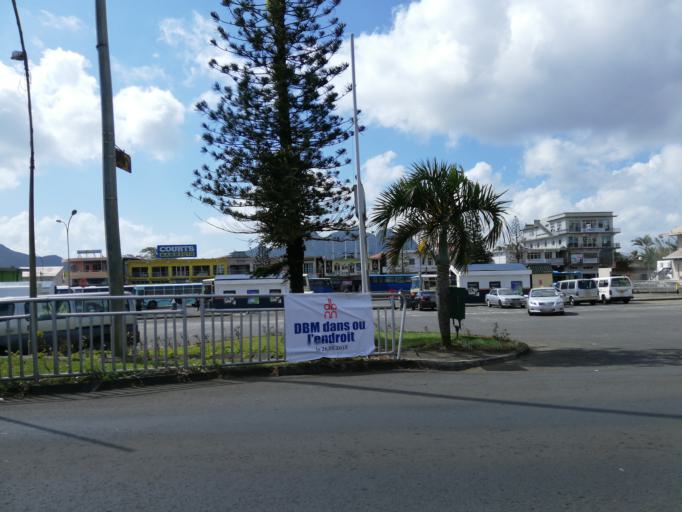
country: MU
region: Moka
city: Verdun
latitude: -20.2257
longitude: 57.5406
